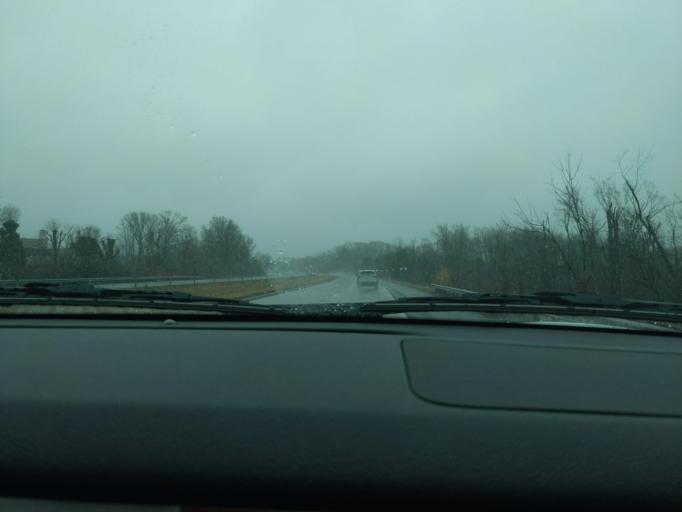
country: US
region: Pennsylvania
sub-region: Bucks County
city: Doylestown
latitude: 40.3089
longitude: -75.1493
